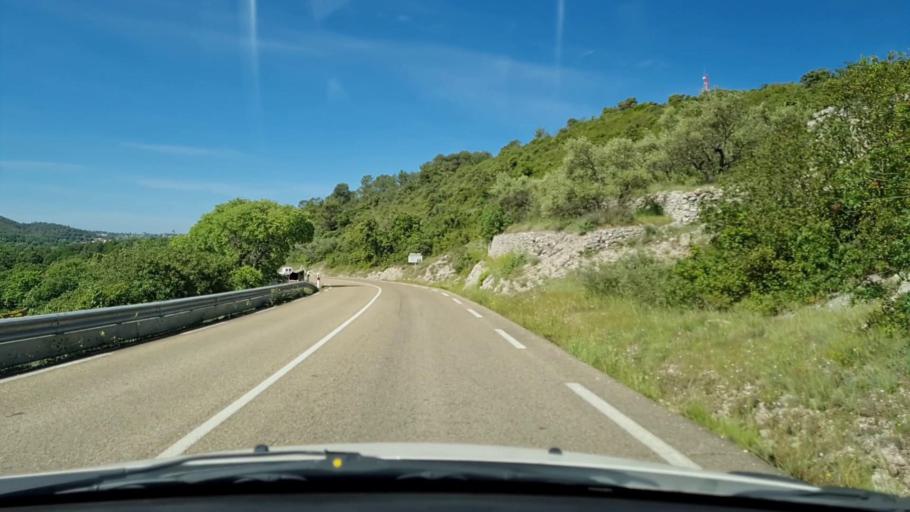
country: FR
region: Languedoc-Roussillon
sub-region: Departement du Gard
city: Vezenobres
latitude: 44.0254
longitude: 4.1521
